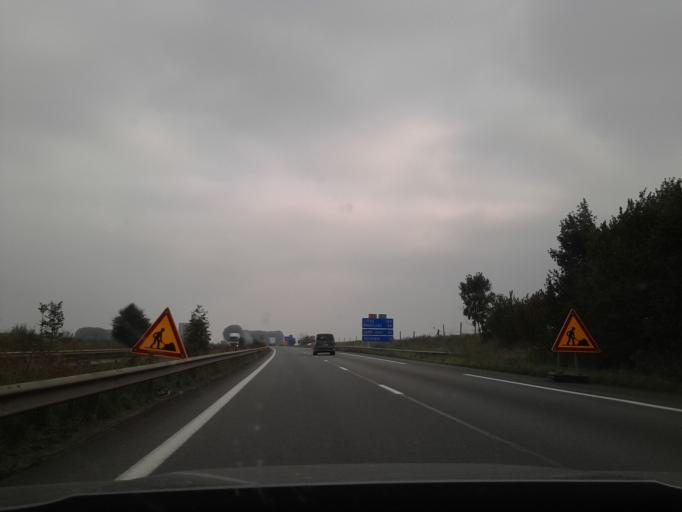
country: FR
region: Nord-Pas-de-Calais
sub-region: Departement du Nord
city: Camphin-en-Pevele
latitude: 50.6013
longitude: 3.2573
